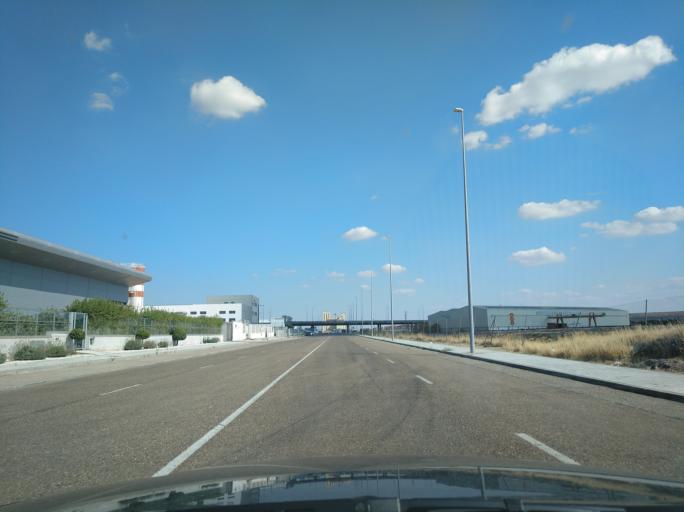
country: ES
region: Extremadura
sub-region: Provincia de Badajoz
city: Badajoz
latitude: 38.8989
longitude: -6.9943
